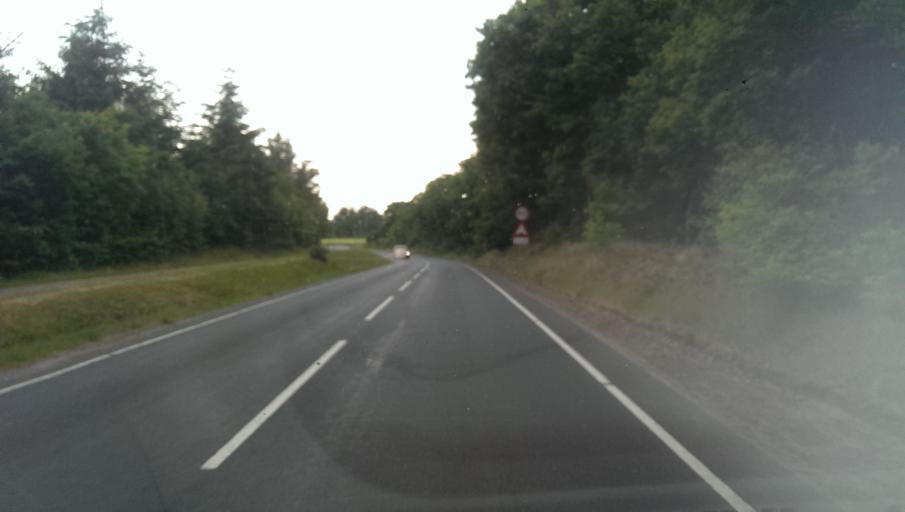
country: DK
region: South Denmark
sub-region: Esbjerg Kommune
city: Bramming
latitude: 55.4283
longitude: 8.6588
